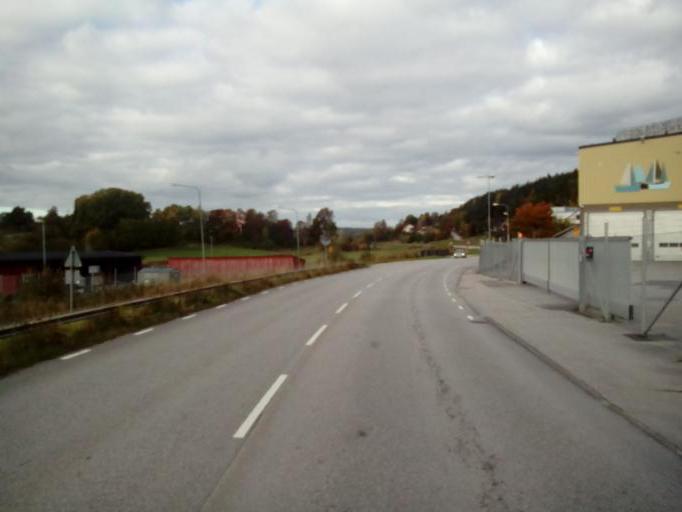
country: SE
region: Kalmar
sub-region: Vasterviks Kommun
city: Gamleby
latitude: 57.9021
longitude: 16.4002
